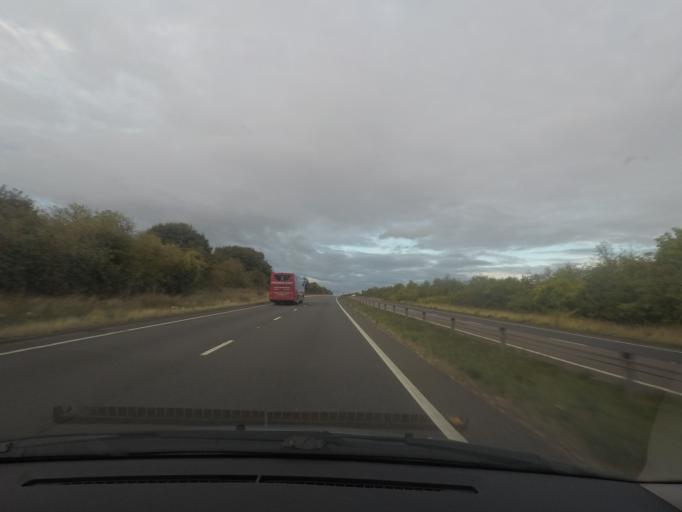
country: GB
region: England
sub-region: Northamptonshire
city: Brackley
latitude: 51.9895
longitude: -1.1677
